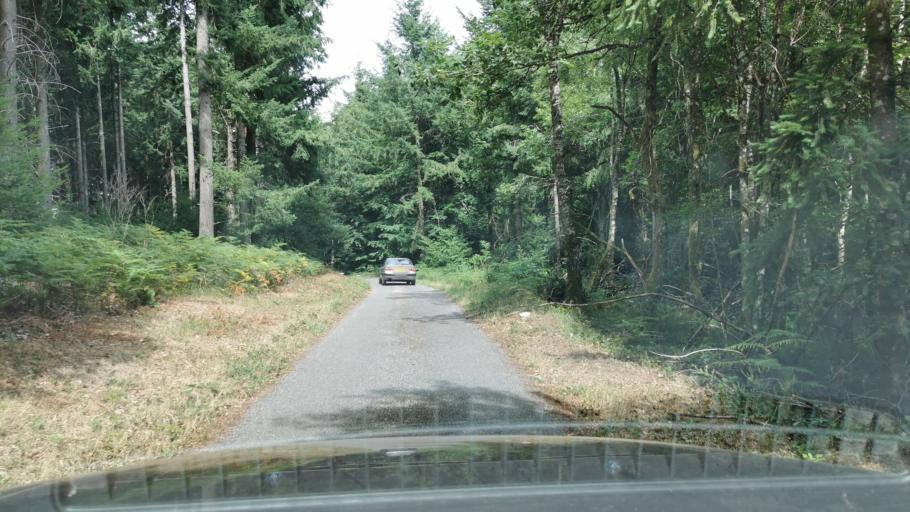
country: FR
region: Bourgogne
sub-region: Departement de Saone-et-Loire
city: Marmagne
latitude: 46.8043
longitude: 4.2754
